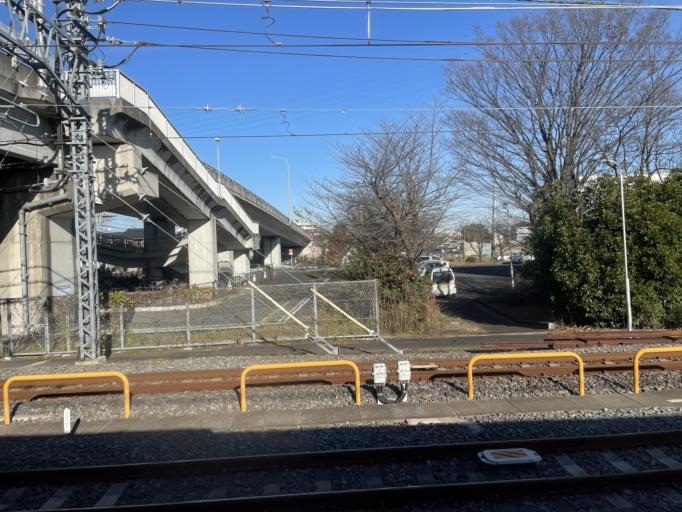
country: JP
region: Saitama
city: Kurihashi
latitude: 36.1119
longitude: 139.7143
